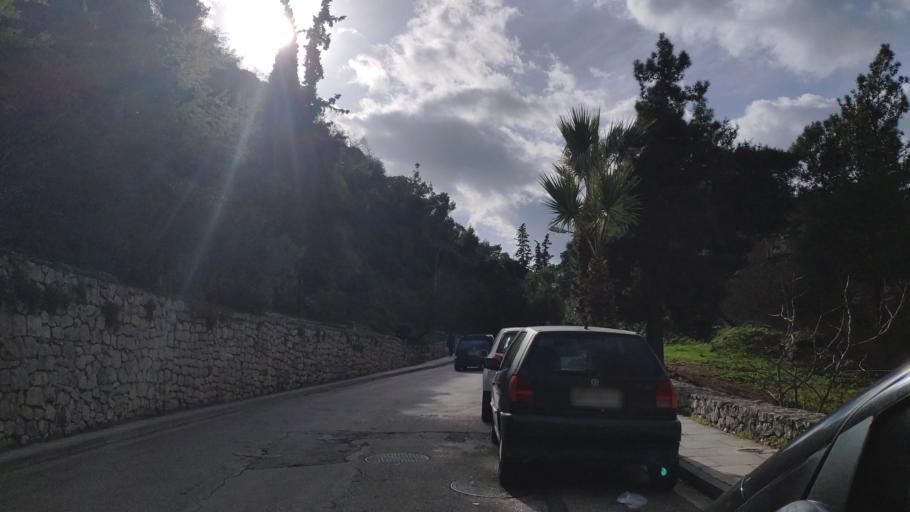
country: GR
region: Peloponnese
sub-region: Nomos Argolidos
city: Nafplio
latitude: 37.5643
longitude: 22.8013
